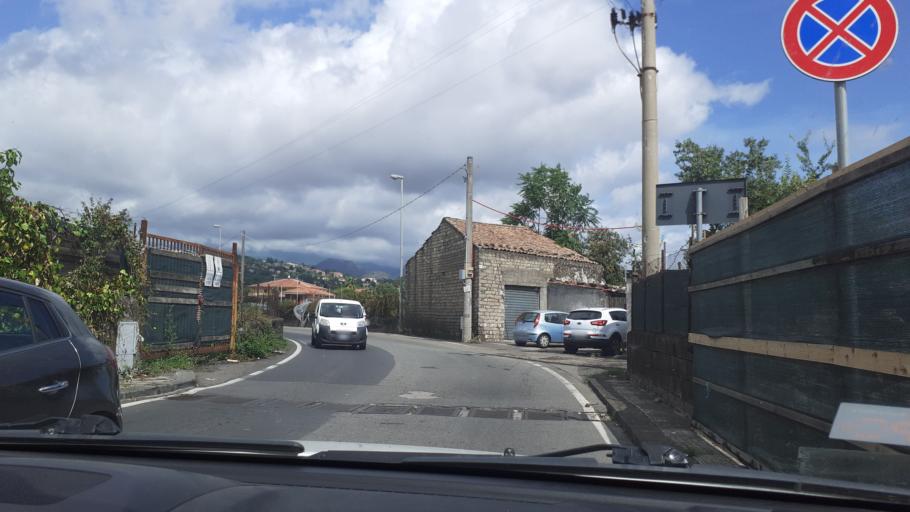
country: IT
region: Sicily
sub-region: Catania
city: San Giovanni la Punta
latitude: 37.5876
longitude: 15.0949
